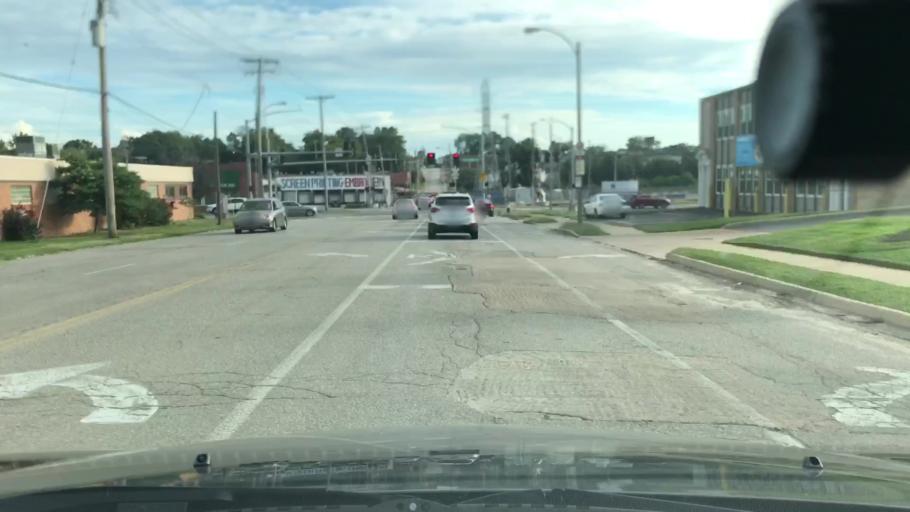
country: US
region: Missouri
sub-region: Saint Louis County
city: Richmond Heights
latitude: 38.6247
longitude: -90.2756
